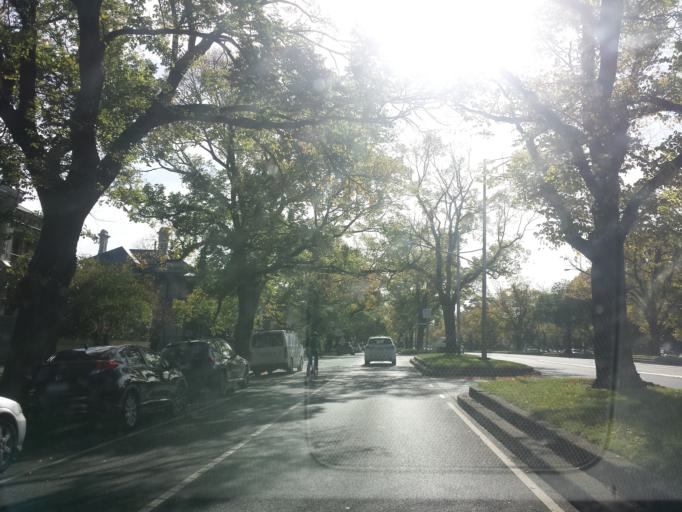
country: AU
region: Victoria
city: Carlton
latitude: -37.7950
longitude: 144.9580
